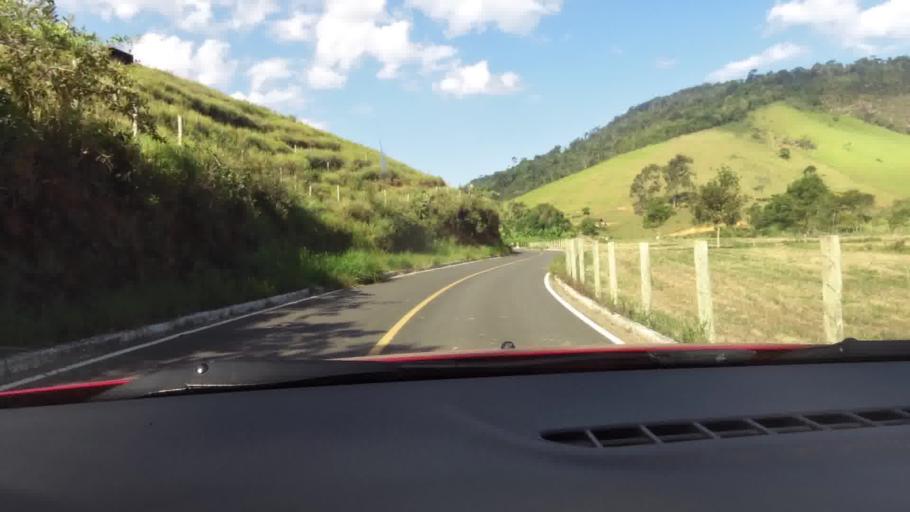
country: BR
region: Espirito Santo
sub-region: Guarapari
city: Guarapari
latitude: -20.5785
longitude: -40.5589
